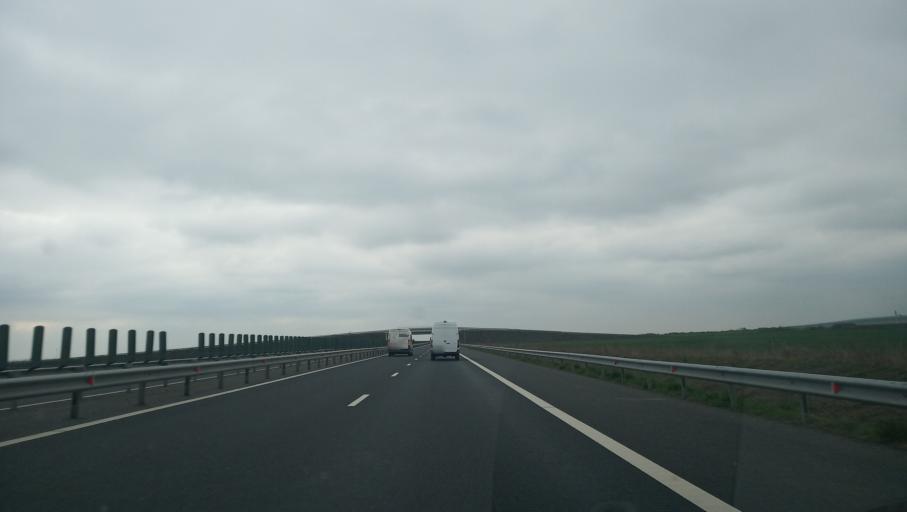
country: RO
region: Timis
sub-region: Oras Recas
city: Recas
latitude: 45.8136
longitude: 21.4996
